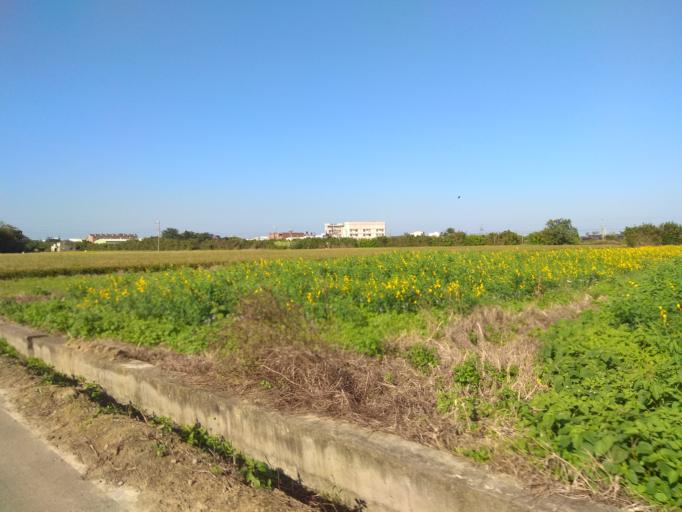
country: TW
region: Taiwan
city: Taoyuan City
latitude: 25.0425
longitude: 121.2250
